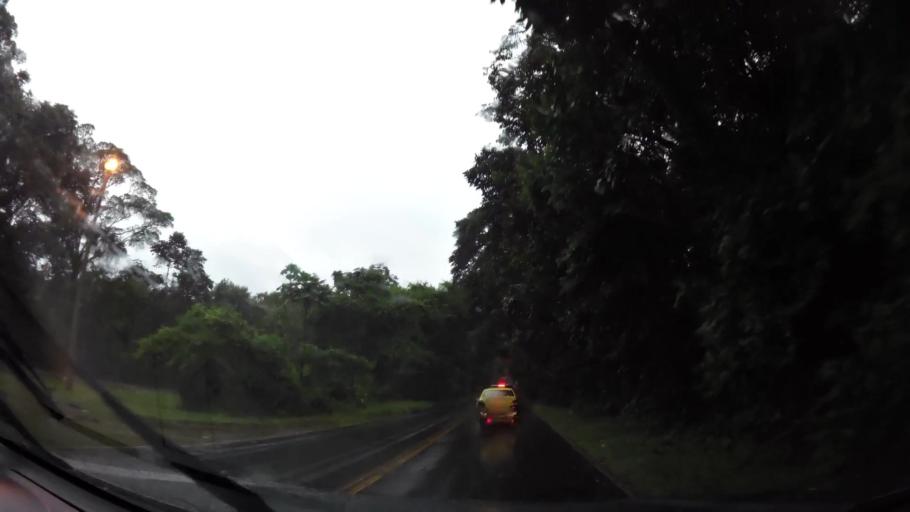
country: PA
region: Panama
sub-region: Distrito de Panama
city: Paraiso
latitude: 9.0055
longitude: -79.5921
